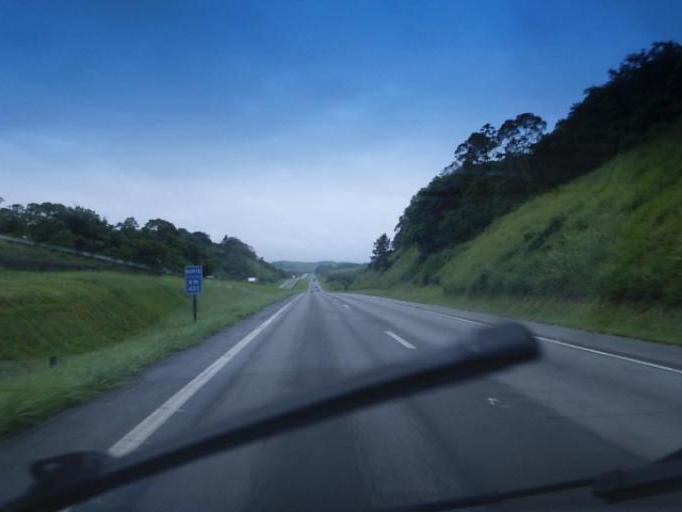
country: BR
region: Sao Paulo
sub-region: Registro
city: Registro
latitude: -24.4411
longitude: -47.7979
